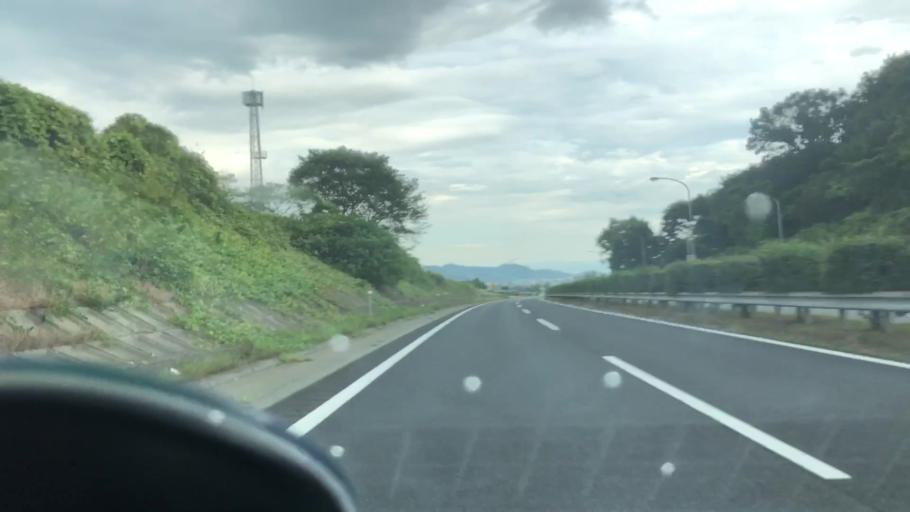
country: JP
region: Hyogo
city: Ono
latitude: 34.9470
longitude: 134.8020
